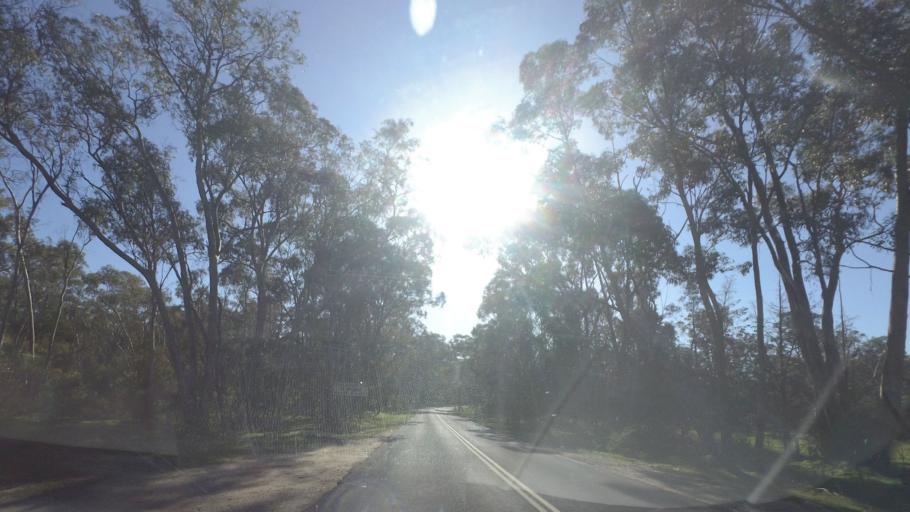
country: AU
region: Victoria
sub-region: Greater Bendigo
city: Kangaroo Flat
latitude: -36.8457
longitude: 144.2810
